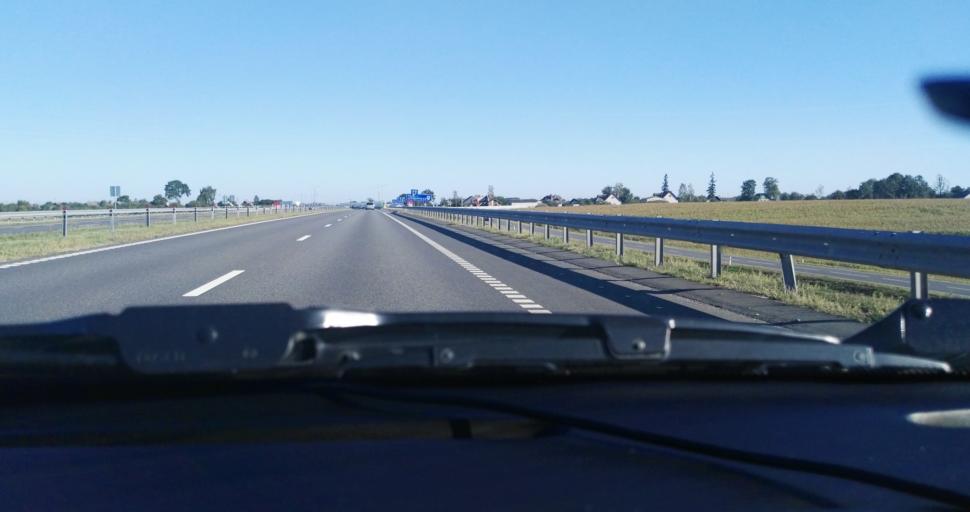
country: BY
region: Gomel
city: Buda-Kashalyova
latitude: 52.5151
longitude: 30.6290
